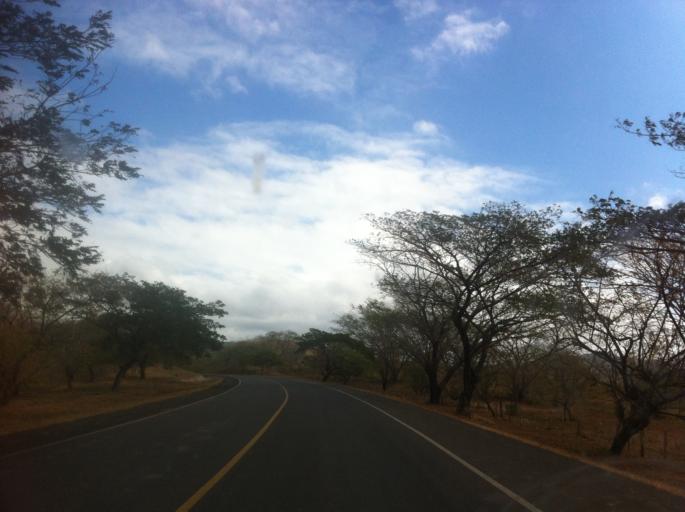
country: NI
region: Chontales
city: Acoyapa
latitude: 11.9918
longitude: -85.1657
